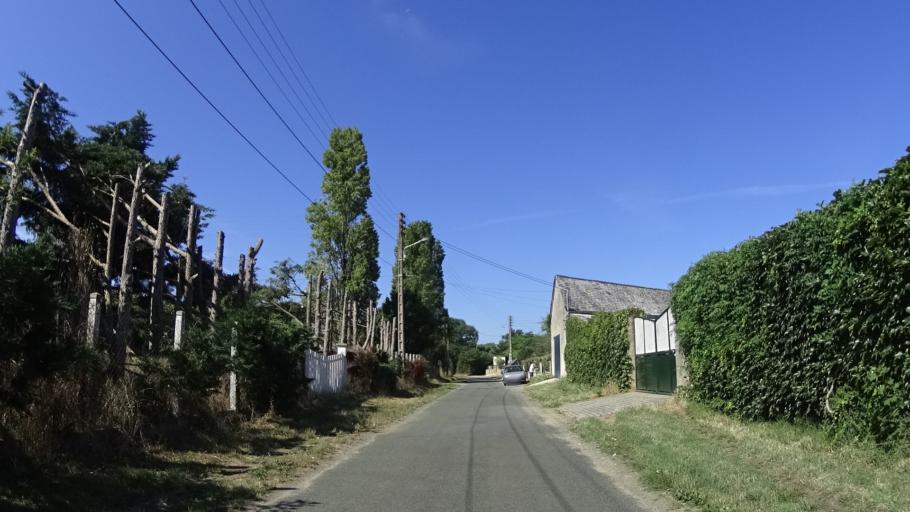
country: FR
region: Pays de la Loire
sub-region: Departement de Maine-et-Loire
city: Tierce
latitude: 47.6174
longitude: -0.5096
